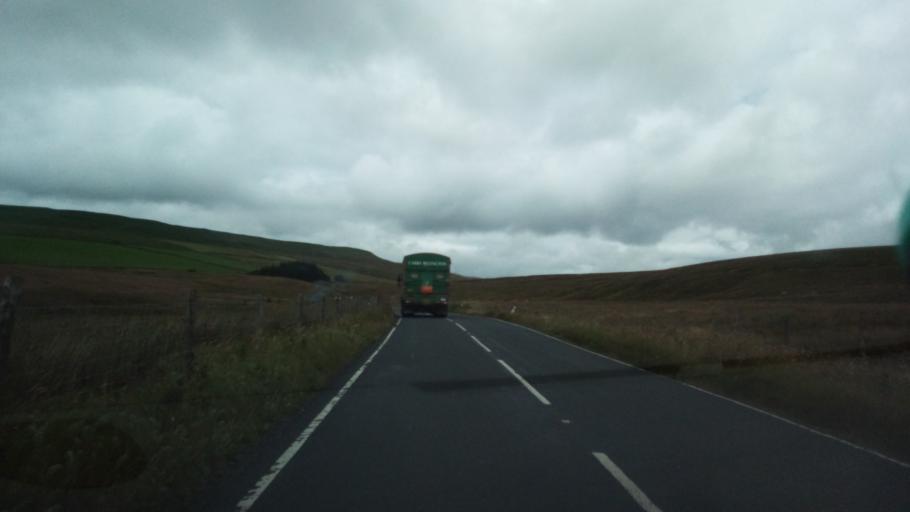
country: GB
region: England
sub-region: North Yorkshire
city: Ingleton
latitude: 54.2460
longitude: -2.3161
